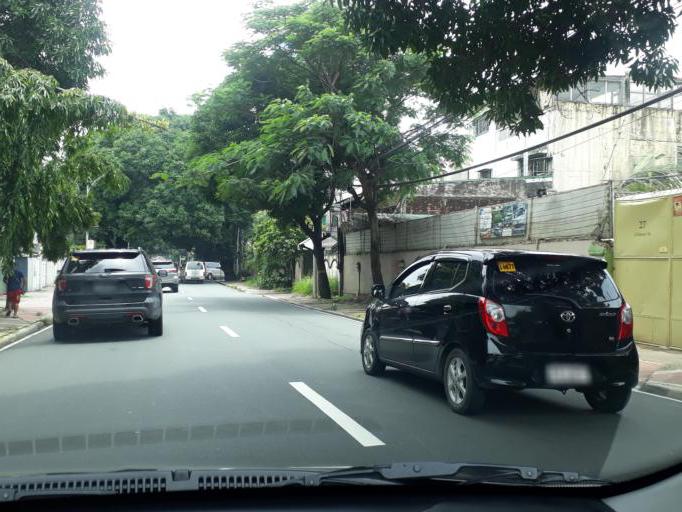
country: PH
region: Metro Manila
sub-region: San Juan
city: San Juan
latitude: 14.6169
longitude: 121.0328
